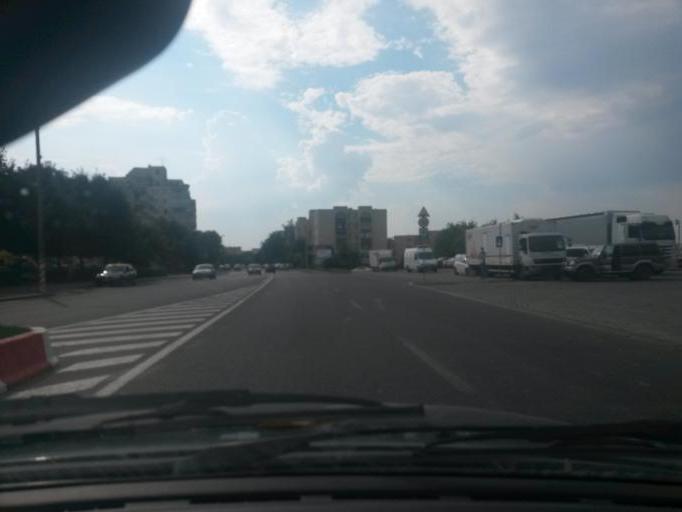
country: RO
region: Mures
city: Targu-Mures
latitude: 46.5336
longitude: 24.5714
